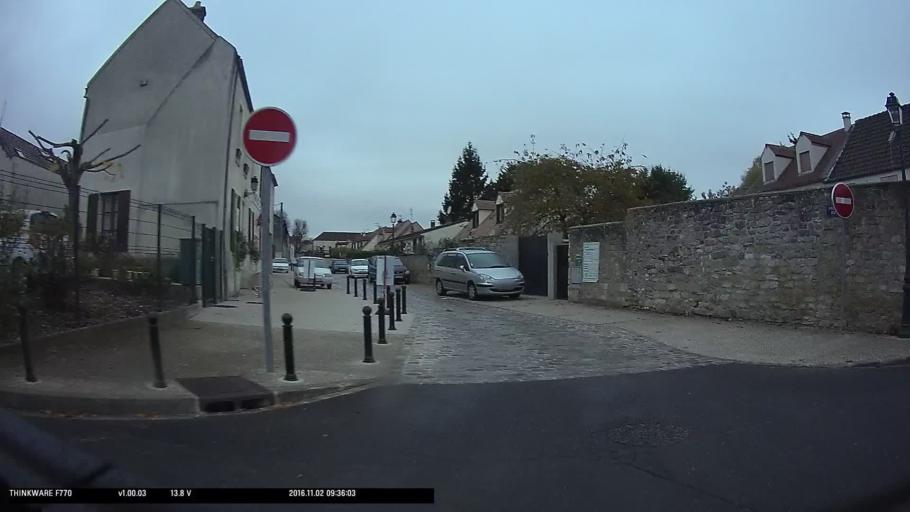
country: FR
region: Ile-de-France
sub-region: Departement du Val-d'Oise
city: Vaureal
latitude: 49.0570
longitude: 2.0224
